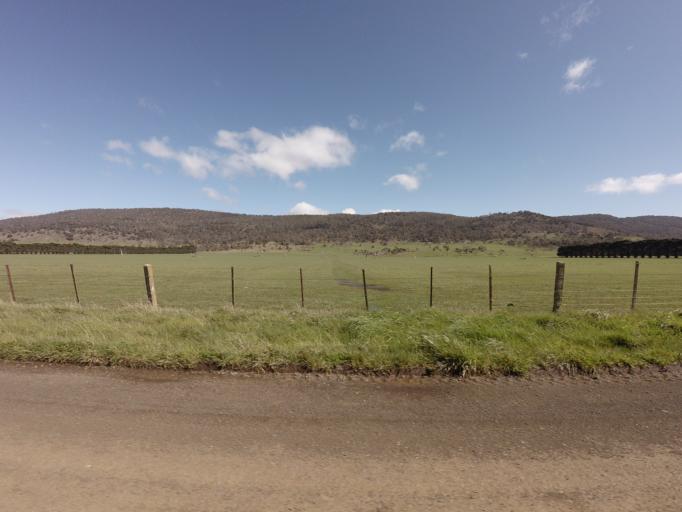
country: AU
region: Tasmania
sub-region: Northern Midlands
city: Evandale
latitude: -41.9597
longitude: 147.4379
